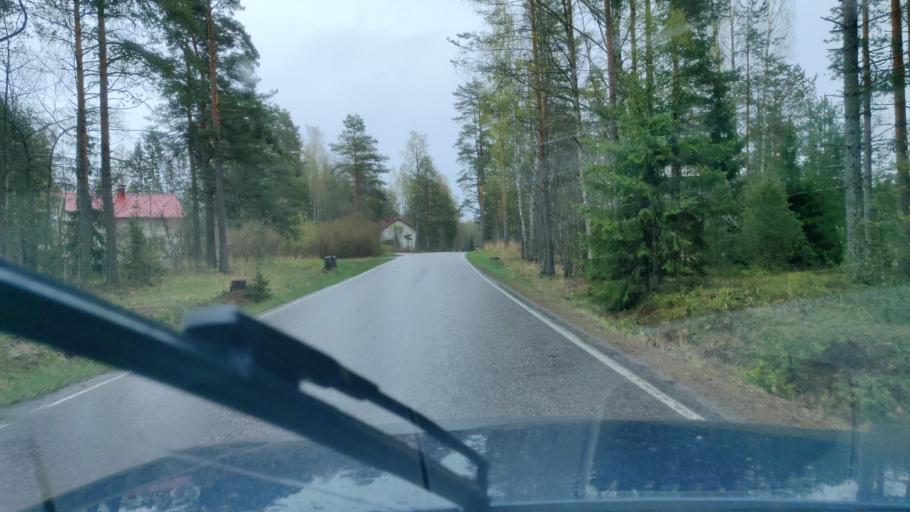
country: FI
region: Uusimaa
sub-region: Helsinki
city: Nurmijaervi
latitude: 60.4998
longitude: 24.6970
